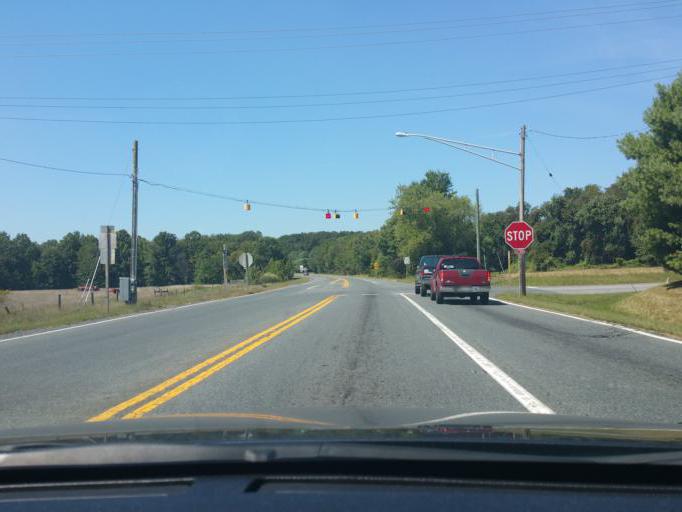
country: US
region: Maryland
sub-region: Harford County
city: Aberdeen
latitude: 39.5766
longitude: -76.1863
